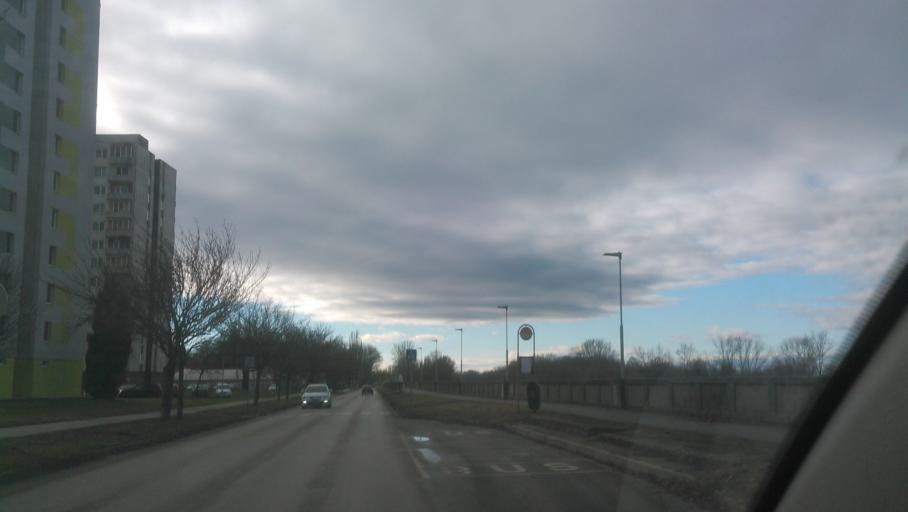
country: SK
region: Trnavsky
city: Hlohovec
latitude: 48.4279
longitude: 17.7915
